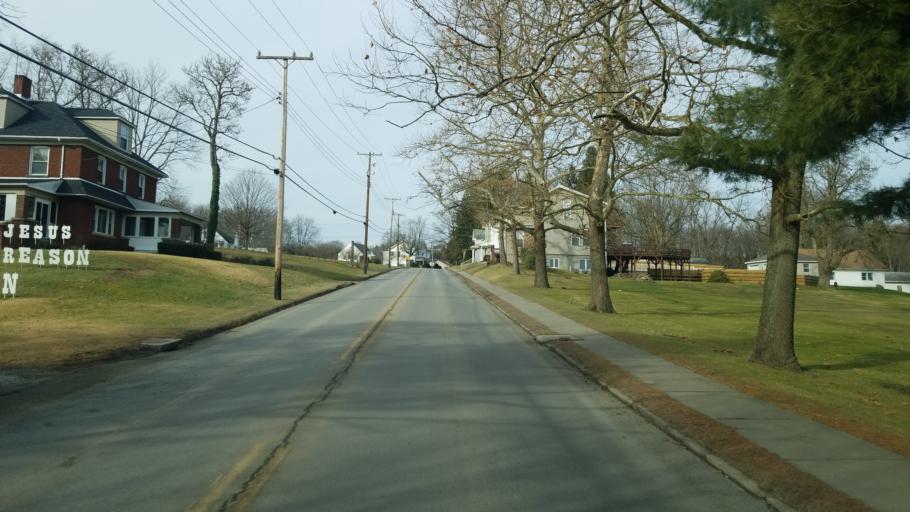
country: US
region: Pennsylvania
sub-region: Jefferson County
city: Punxsutawney
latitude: 40.9484
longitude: -78.9958
